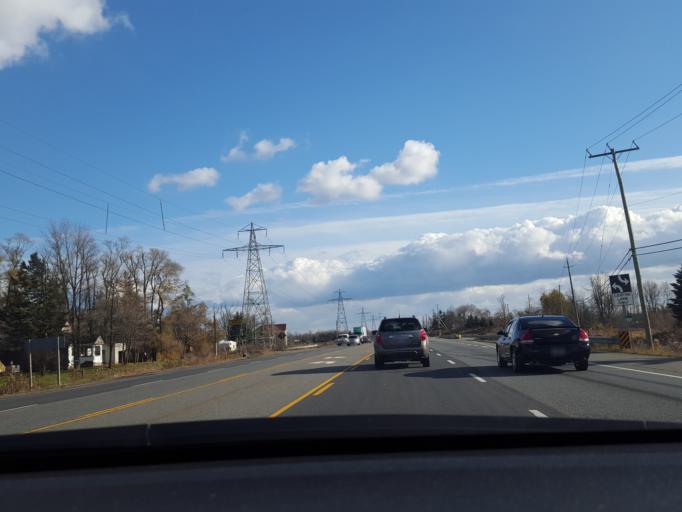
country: CA
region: Ontario
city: Ancaster
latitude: 43.3726
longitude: -80.0000
